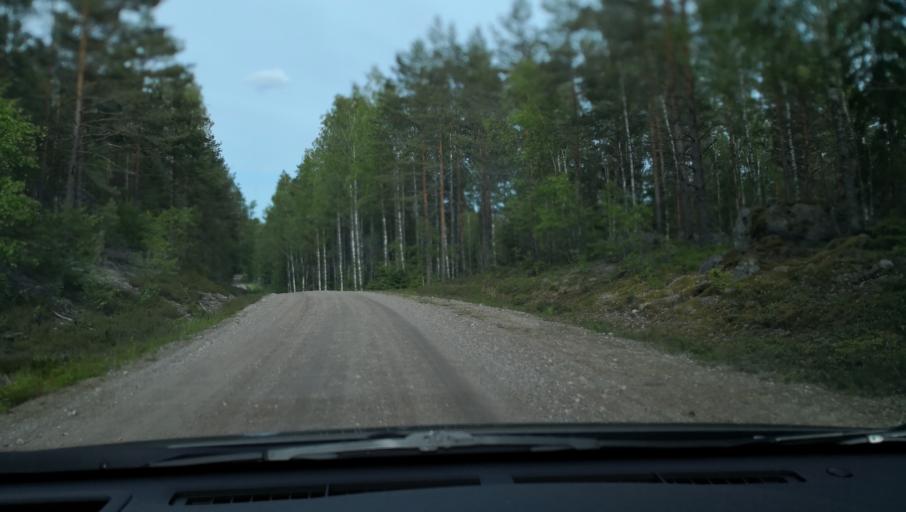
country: SE
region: Vaestmanland
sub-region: Arboga Kommun
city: Tyringe
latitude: 59.3631
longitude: 15.9769
